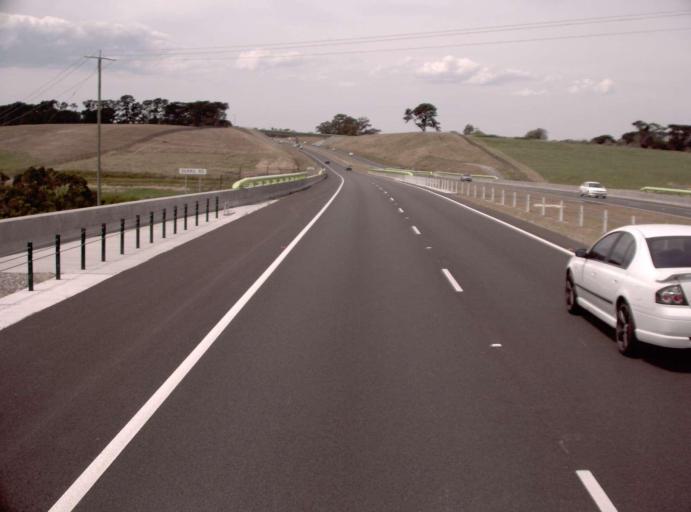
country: AU
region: Victoria
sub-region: Mornington Peninsula
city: Moorooduc
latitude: -38.2669
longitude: 145.1000
